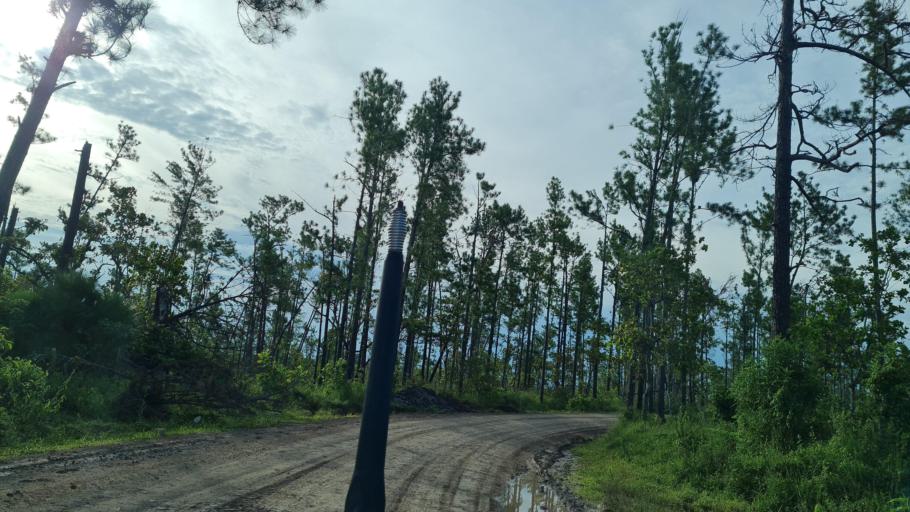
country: NI
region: Atlantico Sur
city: La Cruz de Rio Grande
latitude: 13.5571
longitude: -84.3042
